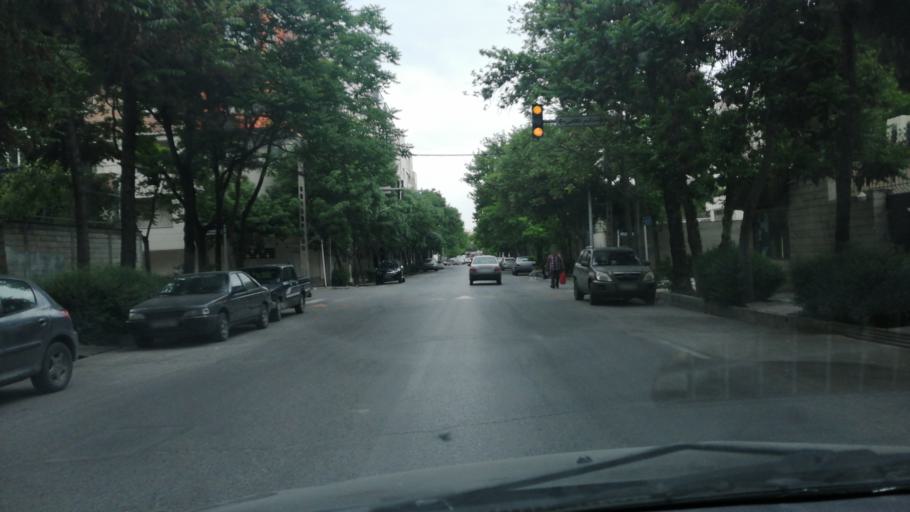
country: IR
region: Razavi Khorasan
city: Mashhad
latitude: 36.2844
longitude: 59.5714
